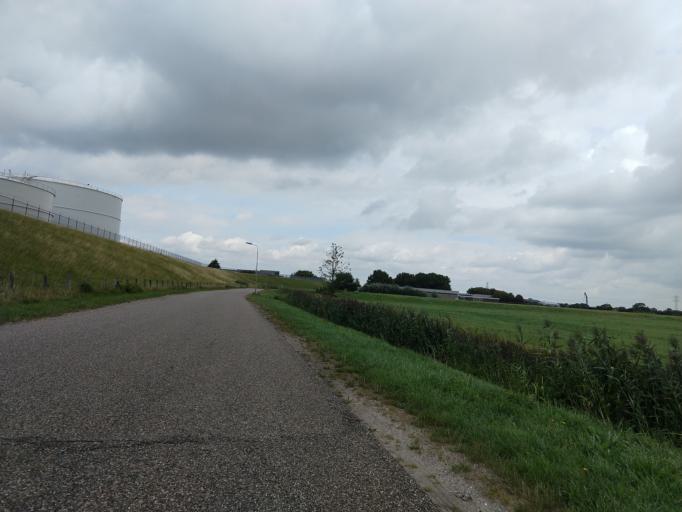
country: NL
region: Zeeland
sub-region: Gemeente Vlissingen
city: Vlissingen
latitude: 51.4471
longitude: 3.6032
